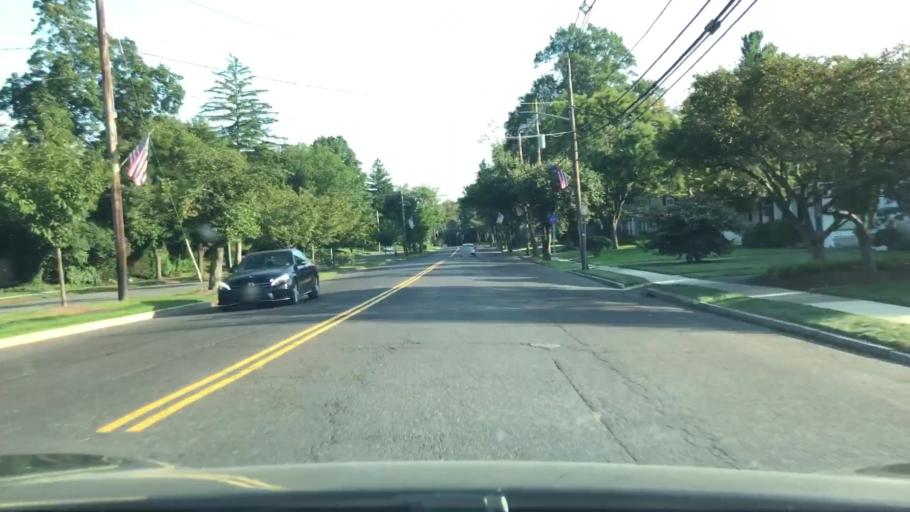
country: US
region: New Jersey
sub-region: Mercer County
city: Pennington
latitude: 40.3205
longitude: -74.7903
